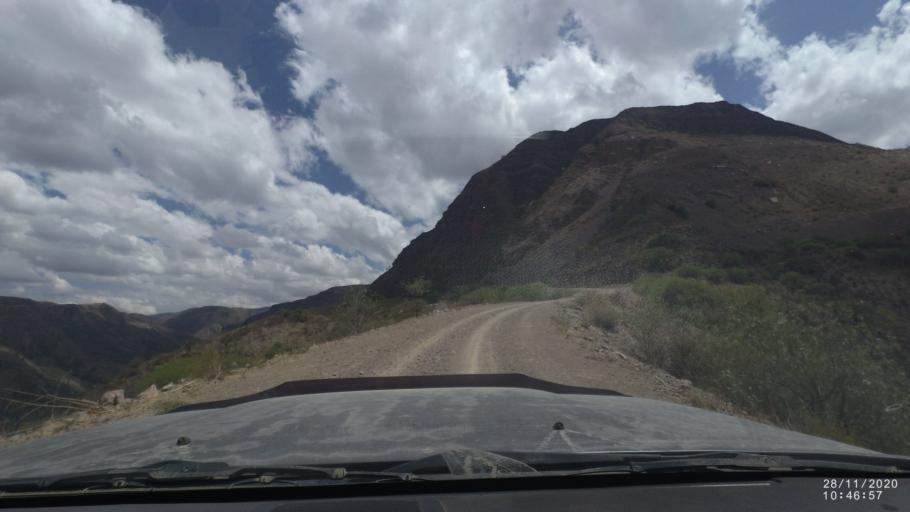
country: BO
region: Cochabamba
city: Capinota
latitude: -17.7870
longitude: -66.1263
